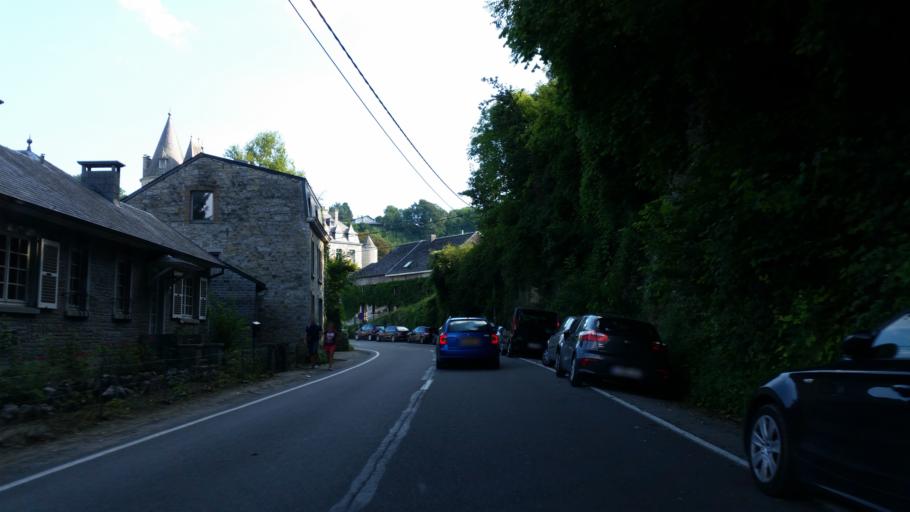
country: BE
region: Wallonia
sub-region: Province du Luxembourg
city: Durbuy
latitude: 50.3540
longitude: 5.4550
